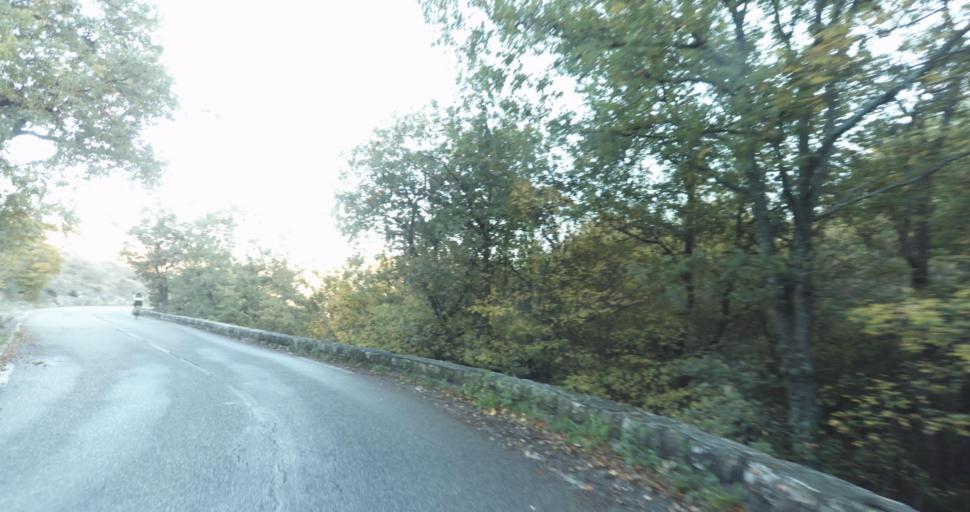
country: FR
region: Provence-Alpes-Cote d'Azur
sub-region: Departement des Alpes-Maritimes
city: Vence
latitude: 43.7524
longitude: 7.0898
